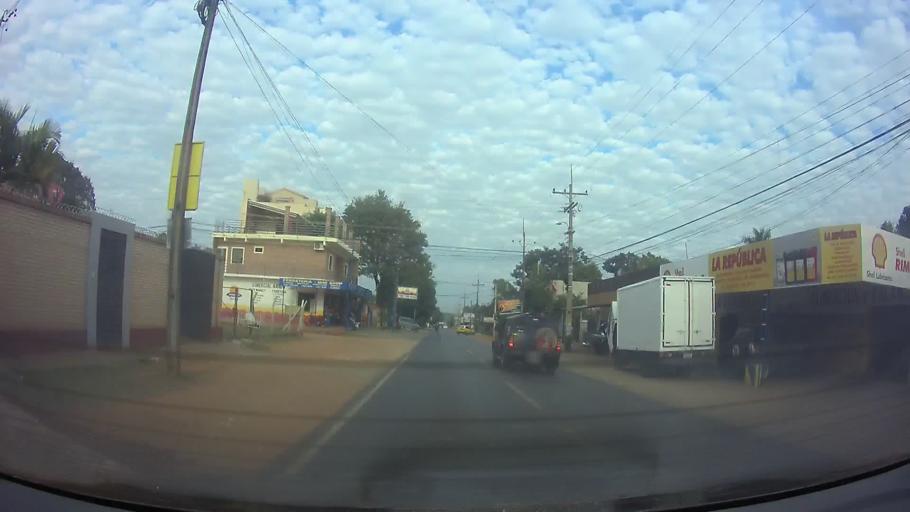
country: PY
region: Central
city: Limpio
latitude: -25.2432
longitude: -57.4784
